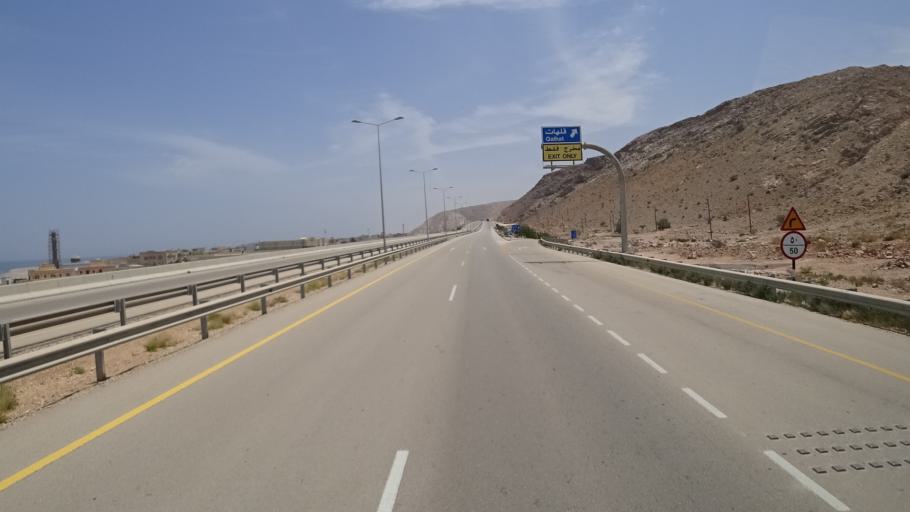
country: OM
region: Ash Sharqiyah
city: Sur
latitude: 22.7075
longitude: 59.3582
